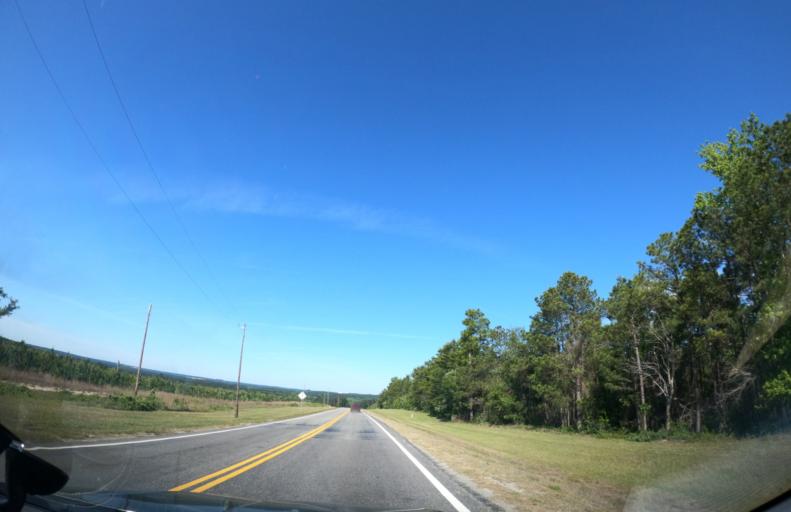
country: US
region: Georgia
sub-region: Columbia County
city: Harlem
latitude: 33.3512
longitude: -82.3388
